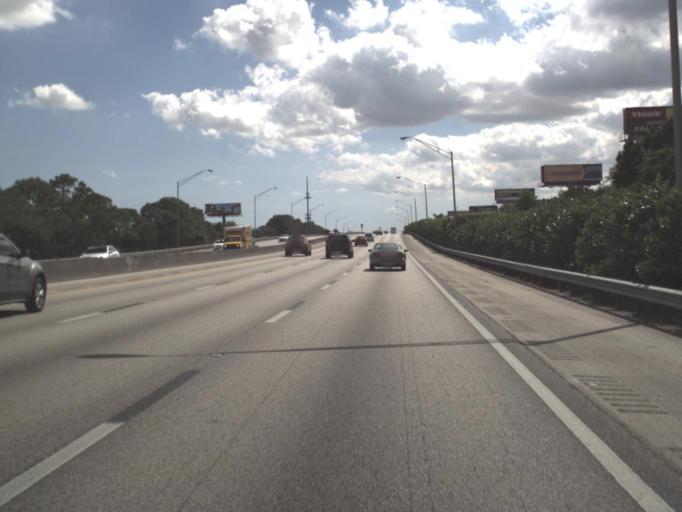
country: US
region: Florida
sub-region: Broward County
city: Davie
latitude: 26.0433
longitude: -80.2145
